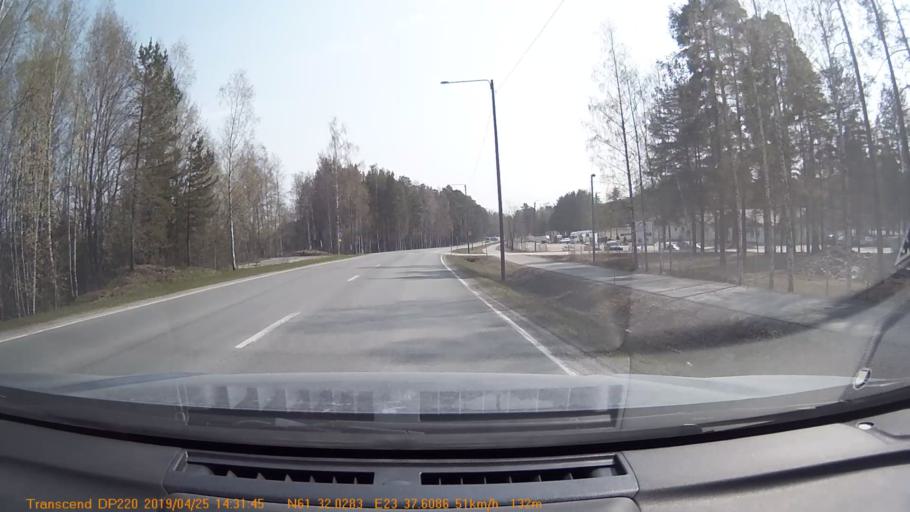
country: FI
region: Pirkanmaa
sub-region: Tampere
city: Yloejaervi
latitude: 61.5339
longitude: 23.6266
